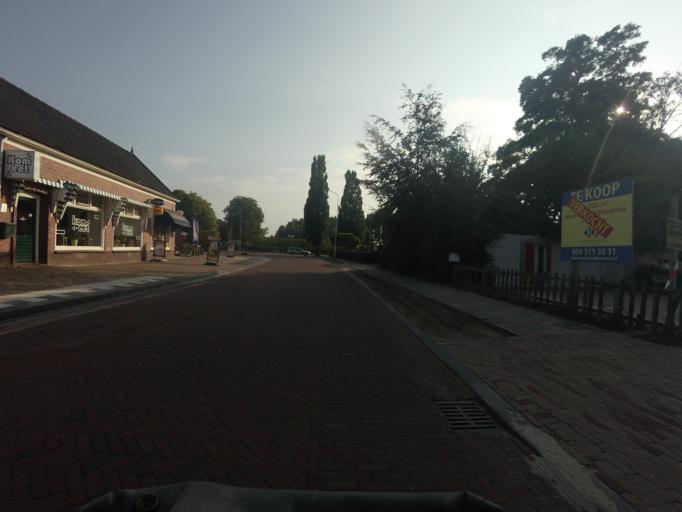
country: NL
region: Groningen
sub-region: Gemeente Haren
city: Haren
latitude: 53.1352
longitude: 6.5636
